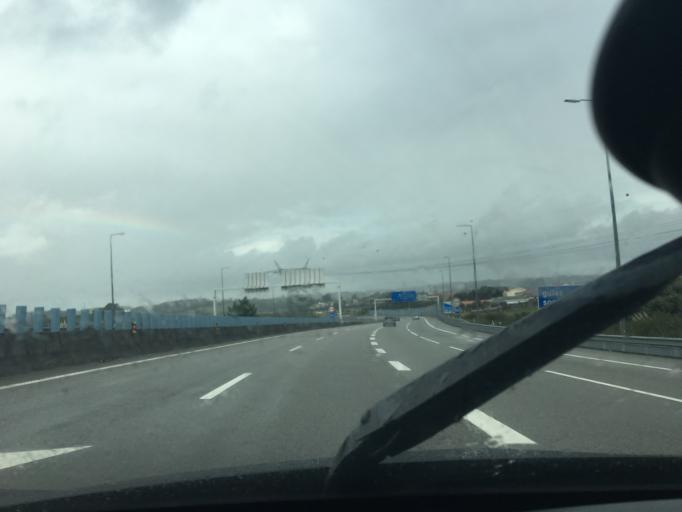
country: PT
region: Porto
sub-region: Matosinhos
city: Guifoes
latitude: 41.2055
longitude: -8.6516
